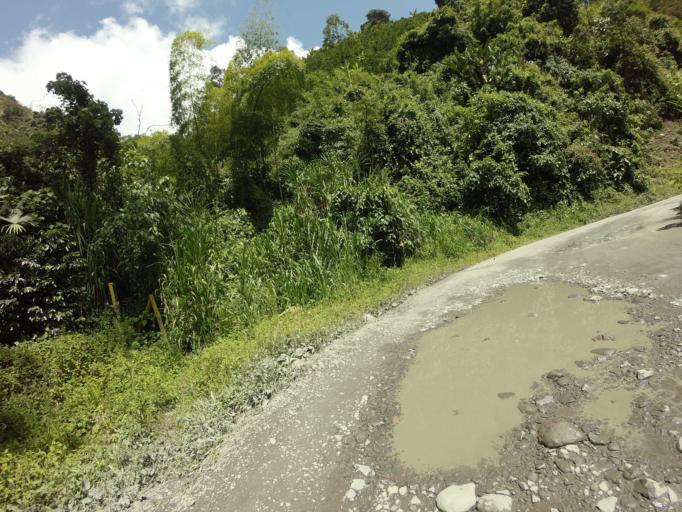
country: CO
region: Caldas
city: Marquetalia
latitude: 5.2920
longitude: -75.0959
